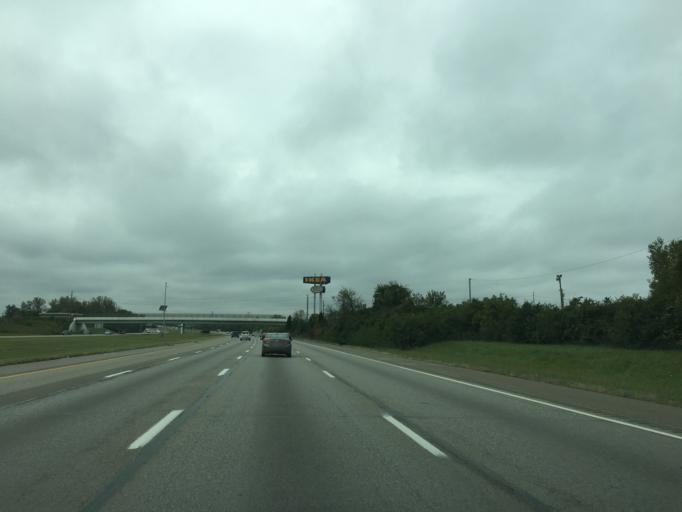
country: US
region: Ohio
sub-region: Butler County
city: Beckett Ridge
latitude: 39.3178
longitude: -84.4292
